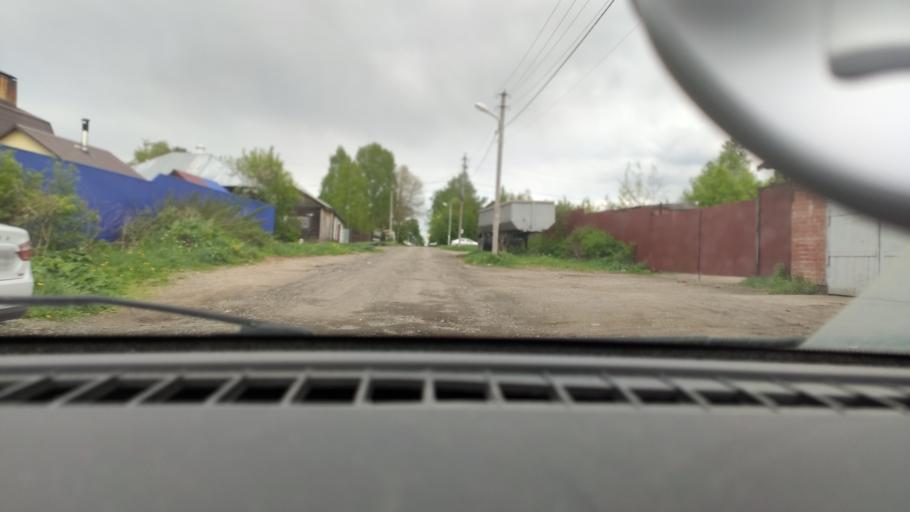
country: RU
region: Perm
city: Perm
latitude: 58.0211
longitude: 56.3283
